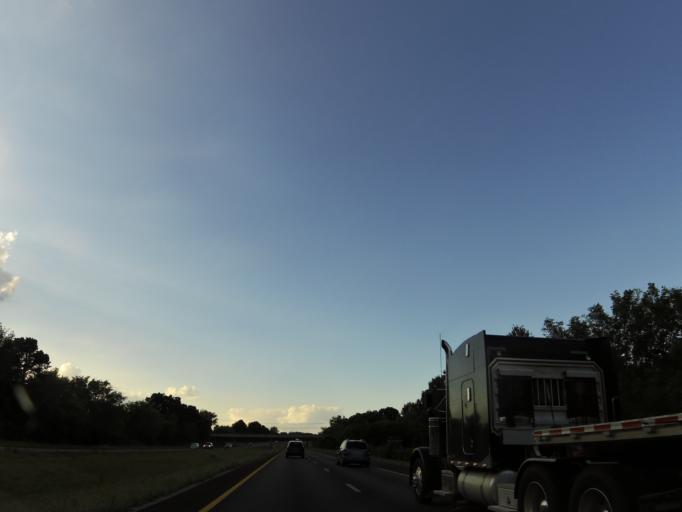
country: US
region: Tennessee
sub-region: Williamson County
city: Thompson's Station
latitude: 35.7870
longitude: -86.8616
